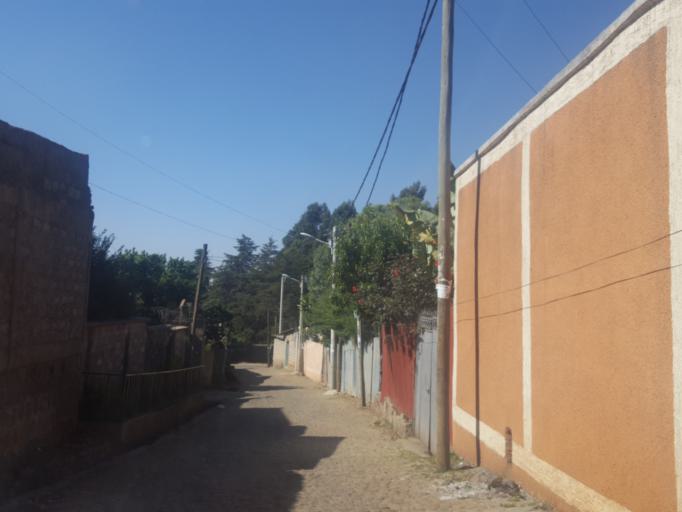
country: ET
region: Adis Abeba
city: Addis Ababa
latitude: 9.0541
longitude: 38.7246
